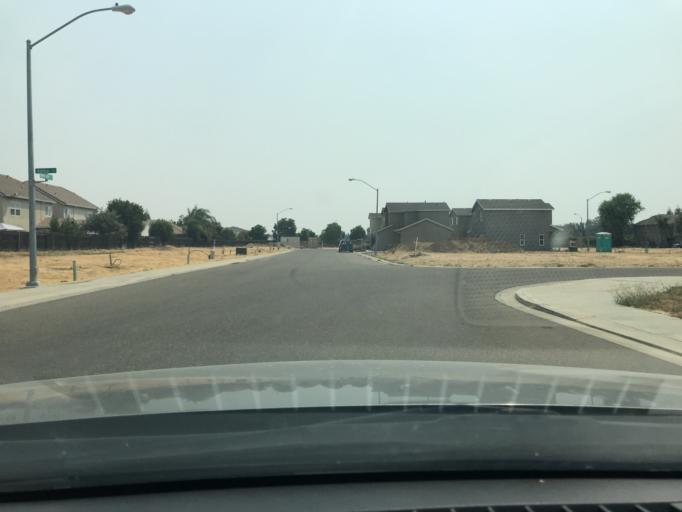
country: US
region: California
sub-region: Merced County
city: Merced
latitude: 37.3336
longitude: -120.4973
